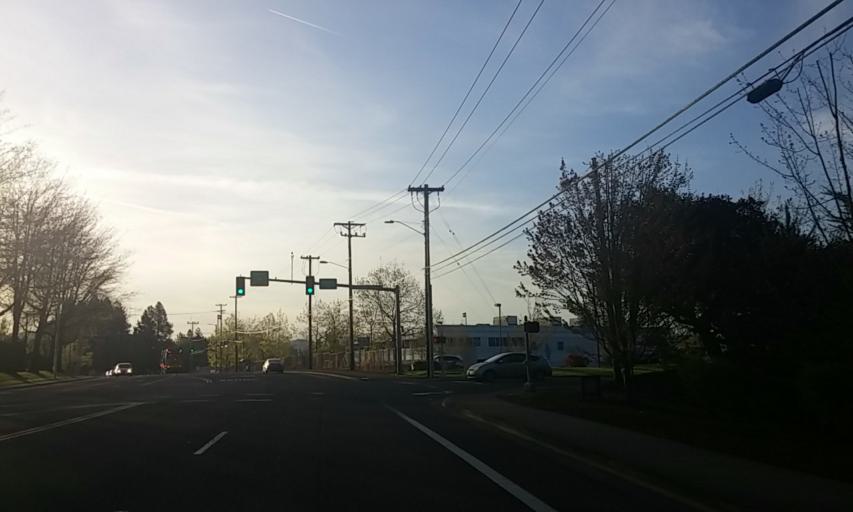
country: US
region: Oregon
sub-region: Washington County
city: Cedar Mill
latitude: 45.5308
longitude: -122.8264
